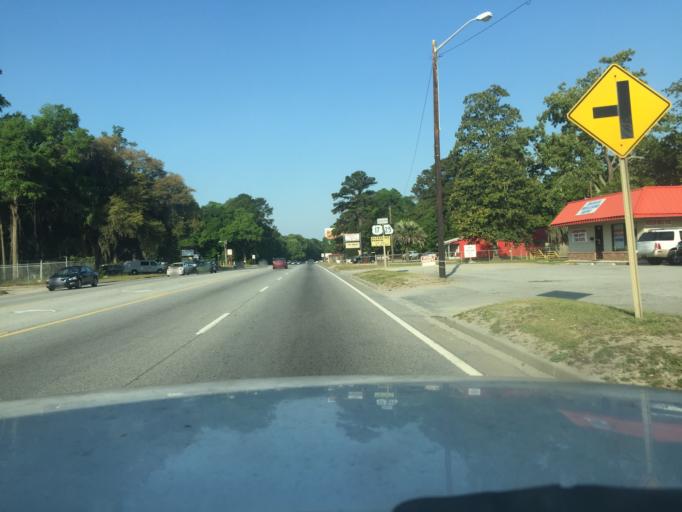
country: US
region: Georgia
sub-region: Chatham County
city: Georgetown
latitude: 32.0419
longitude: -81.1918
